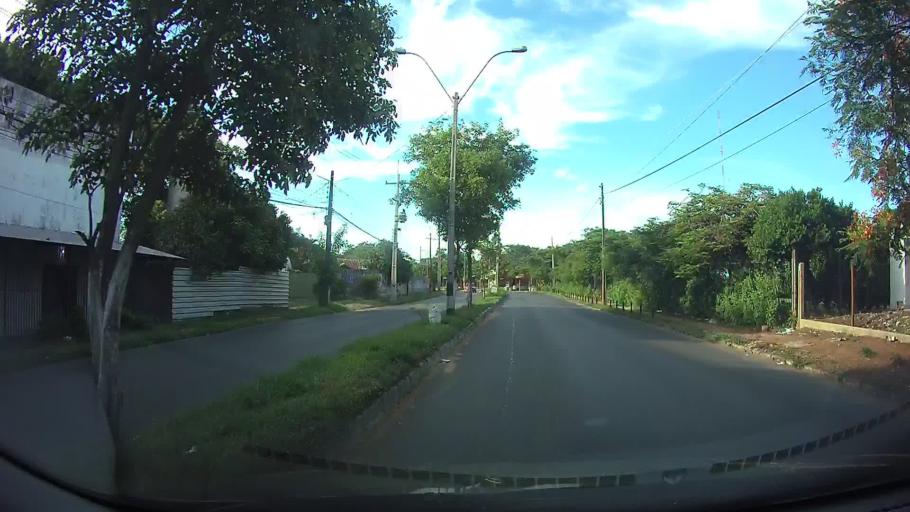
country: PY
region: Central
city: Villa Elisa
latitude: -25.3881
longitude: -57.5829
